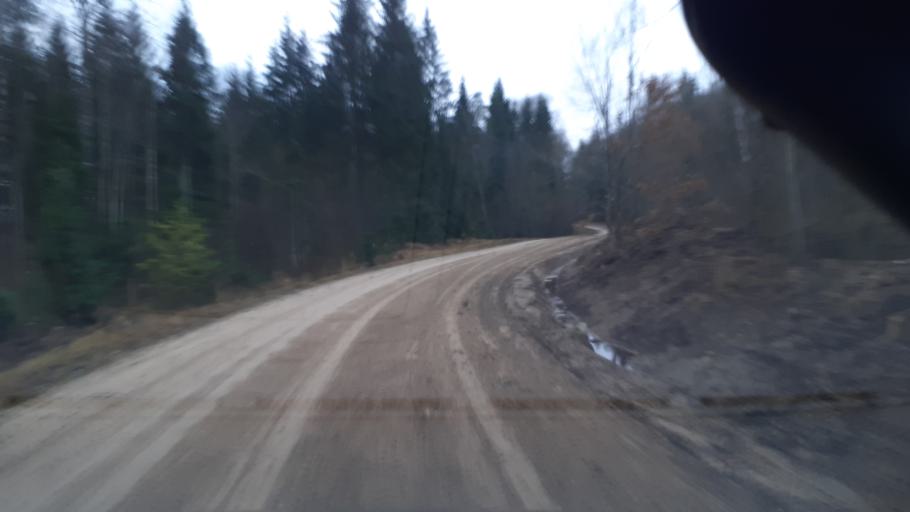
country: LV
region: Kuldigas Rajons
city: Kuldiga
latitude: 56.9166
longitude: 21.7714
